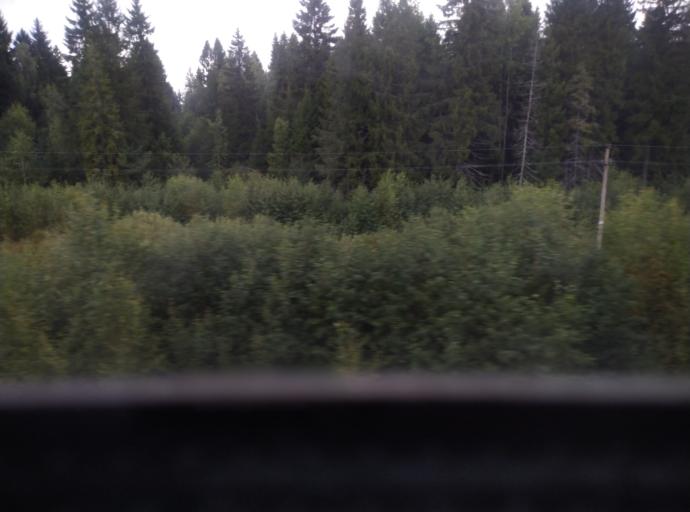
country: RU
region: Jaroslavl
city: Burmakino
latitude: 57.4368
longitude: 40.3334
